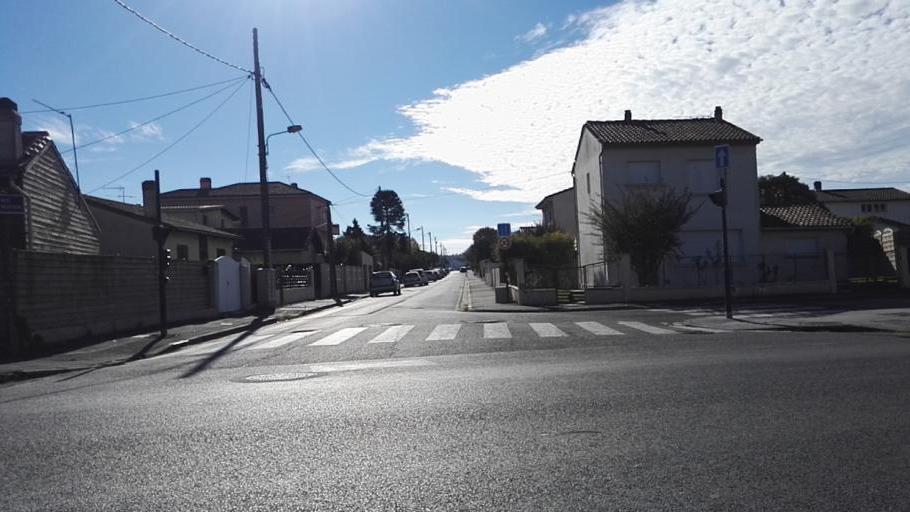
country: FR
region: Aquitaine
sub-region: Departement de la Gironde
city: Eysines
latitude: 44.8601
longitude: -0.6341
